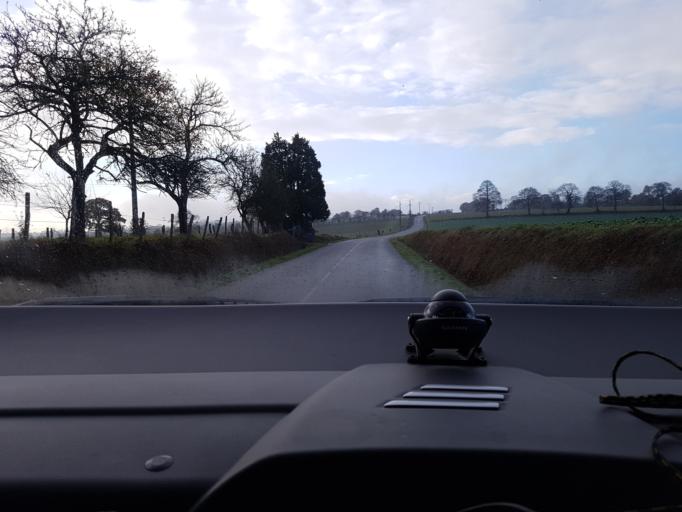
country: FR
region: Brittany
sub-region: Departement d'Ille-et-Vilaine
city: La Bouexiere
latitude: 48.1917
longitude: -1.4238
